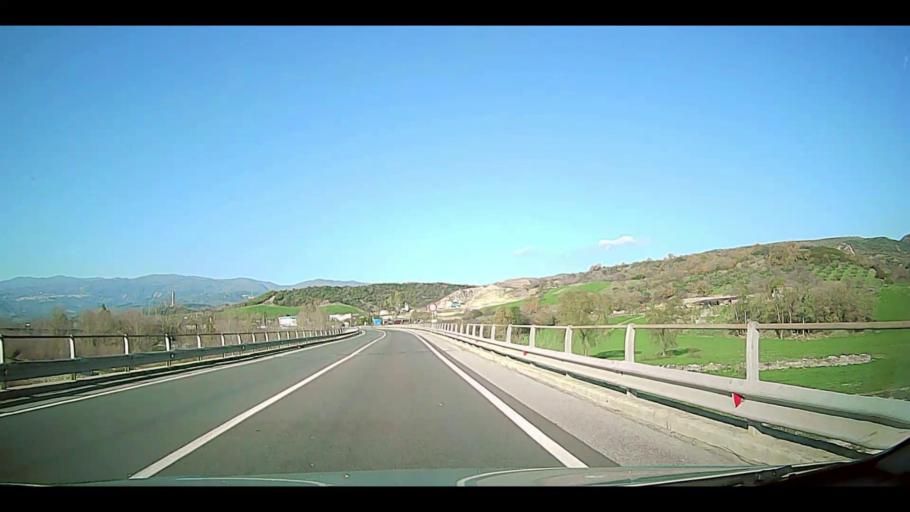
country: IT
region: Calabria
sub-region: Provincia di Crotone
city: Belvedere Spinello
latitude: 39.1882
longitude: 16.8524
